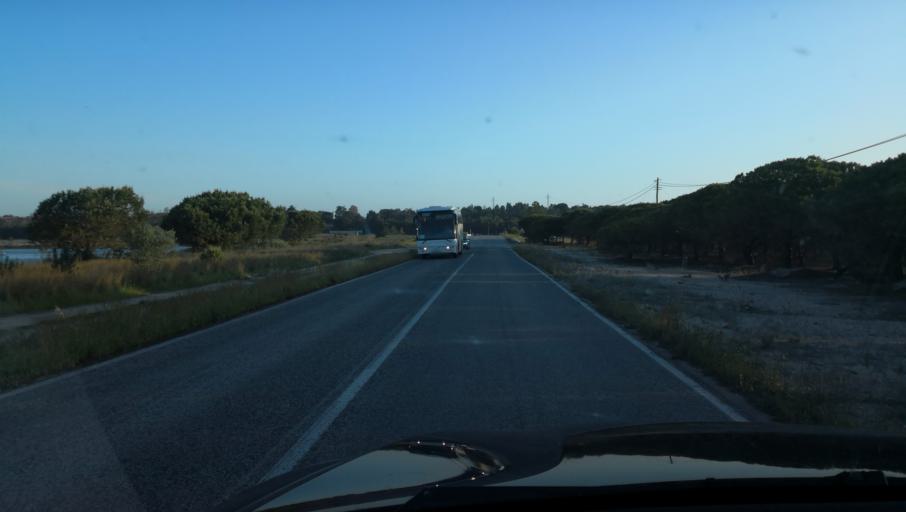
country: PT
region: Setubal
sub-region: Setubal
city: Setubal
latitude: 38.4843
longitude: -8.7931
